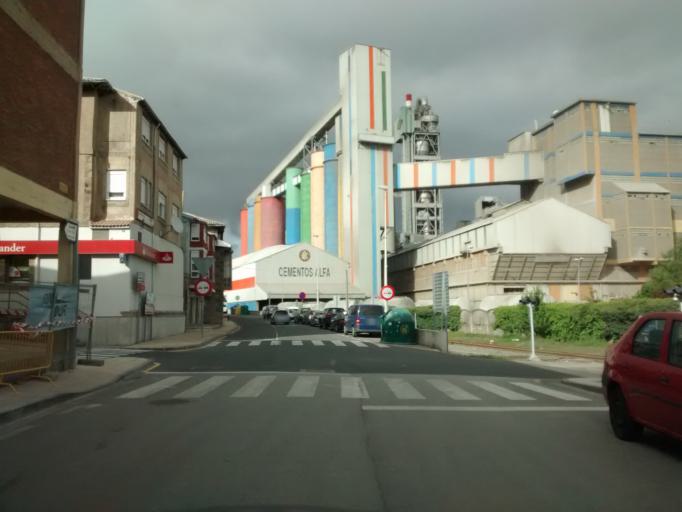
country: ES
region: Cantabria
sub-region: Provincia de Cantabria
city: Mataporquera
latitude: 42.8738
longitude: -4.1631
